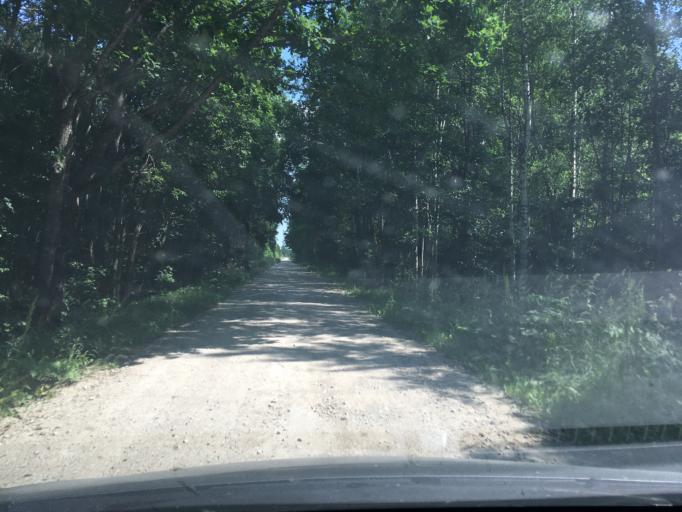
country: EE
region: Raplamaa
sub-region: Maerjamaa vald
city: Marjamaa
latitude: 58.8099
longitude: 24.4428
